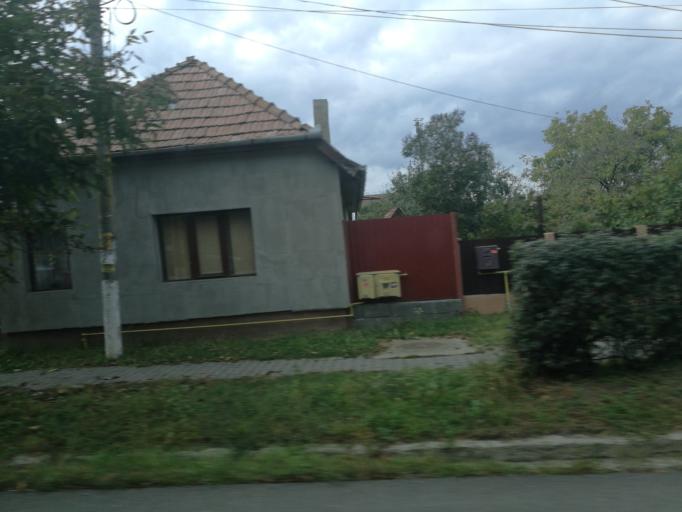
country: RO
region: Mures
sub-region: Comuna Cristesti
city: Cristesti
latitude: 46.5037
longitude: 24.4946
